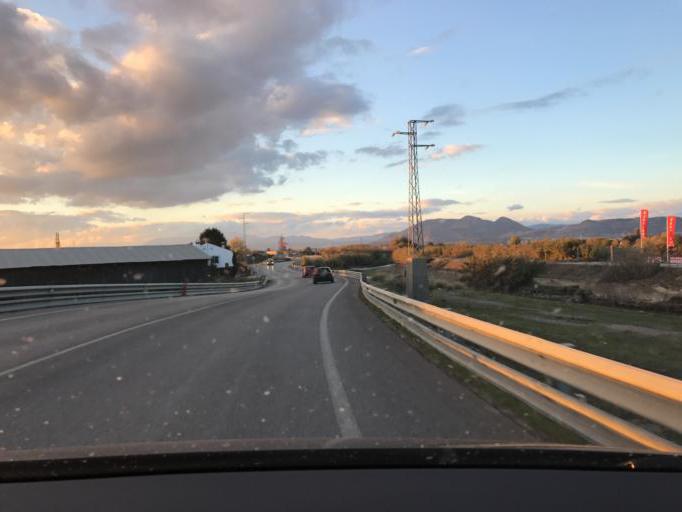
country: ES
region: Andalusia
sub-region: Provincia de Granada
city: Cullar-Vega
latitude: 37.1731
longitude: -3.6551
